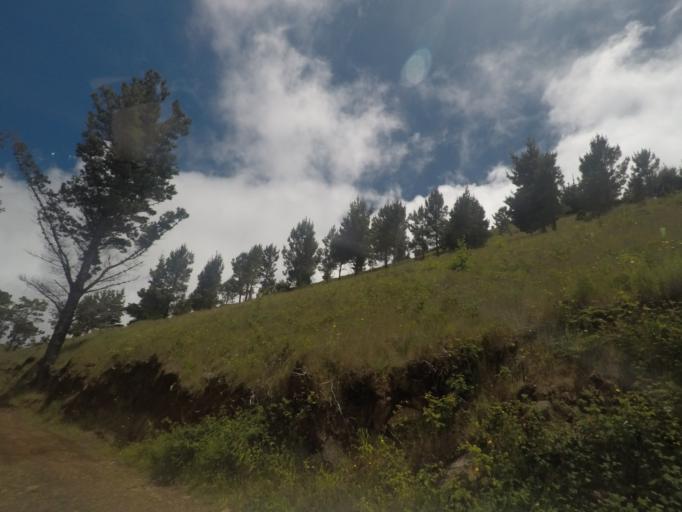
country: PT
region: Madeira
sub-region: Funchal
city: Nossa Senhora do Monte
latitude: 32.7040
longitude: -16.9050
